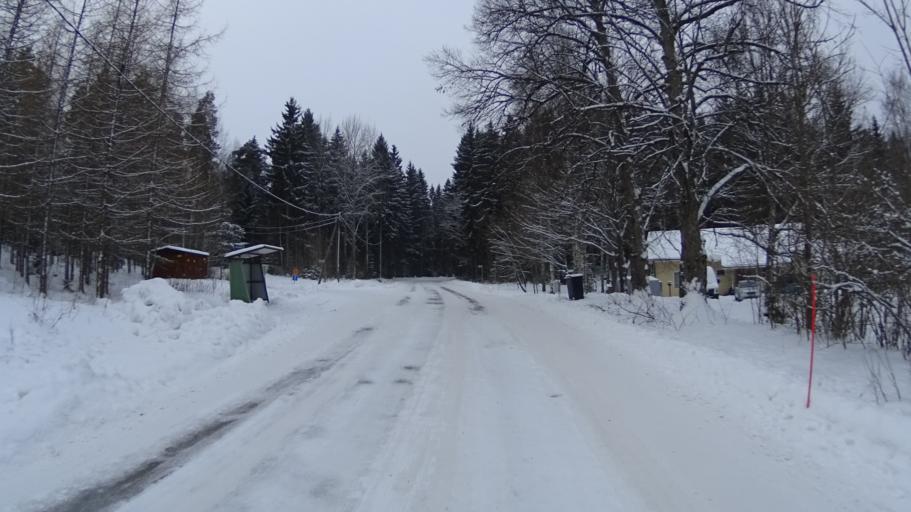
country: FI
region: Uusimaa
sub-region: Helsinki
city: Vihti
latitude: 60.3367
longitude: 24.2727
